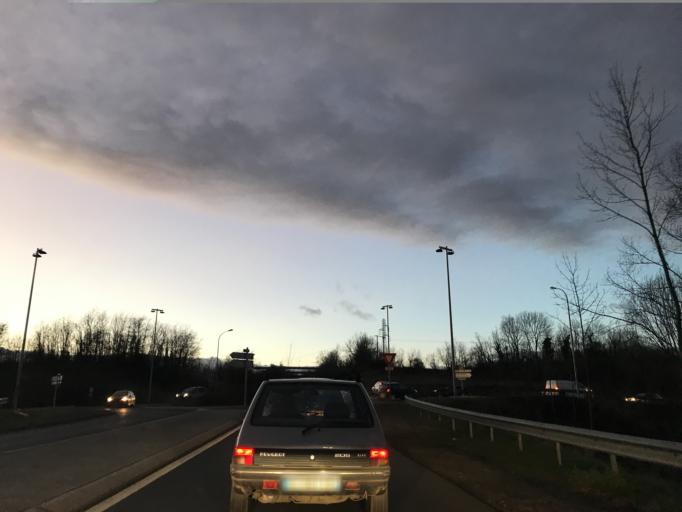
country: FR
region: Auvergne
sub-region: Departement du Puy-de-Dome
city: Dallet
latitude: 45.7749
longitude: 3.2353
